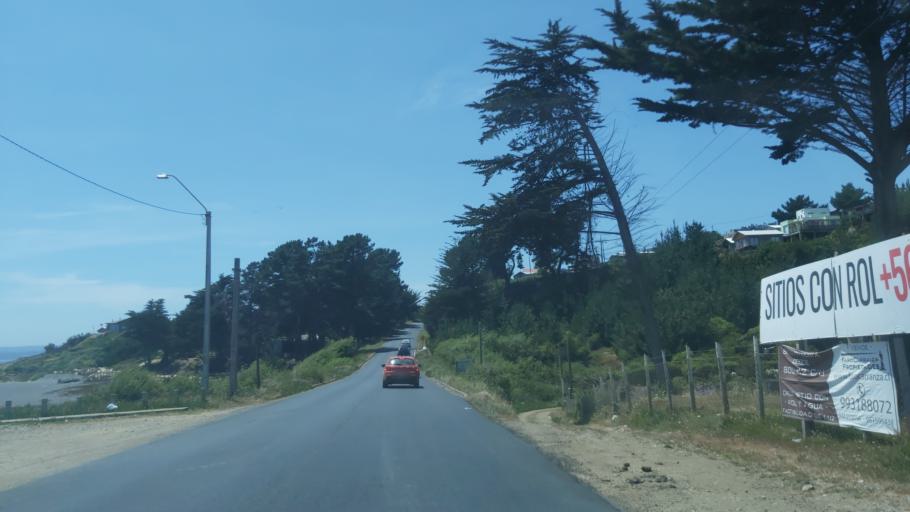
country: CL
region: Maule
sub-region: Provincia de Cauquenes
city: Cauquenes
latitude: -35.8262
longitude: -72.6108
